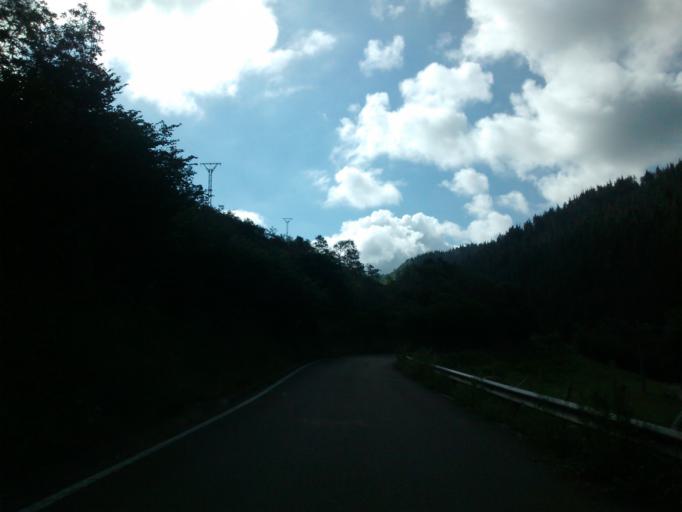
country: ES
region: Cantabria
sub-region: Provincia de Cantabria
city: Ruente
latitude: 43.1963
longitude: -4.2914
